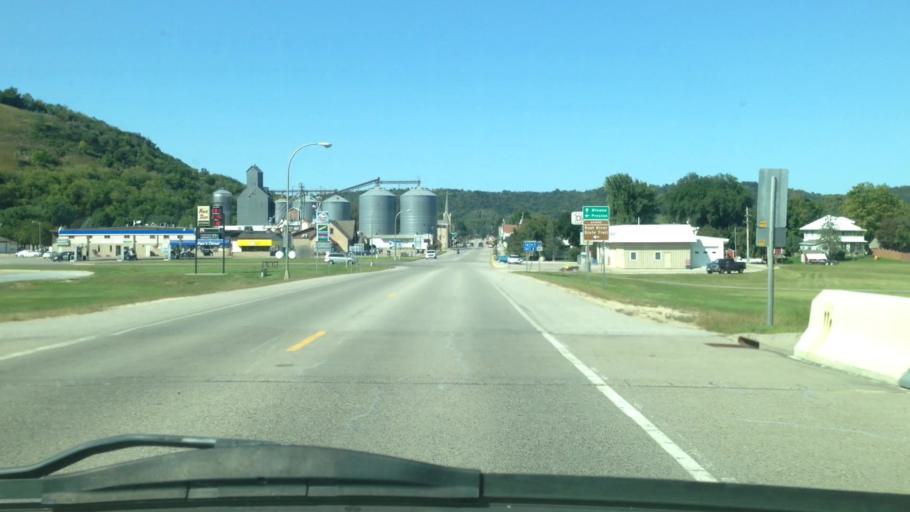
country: US
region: Minnesota
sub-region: Fillmore County
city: Rushford
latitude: 43.8041
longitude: -91.7532
